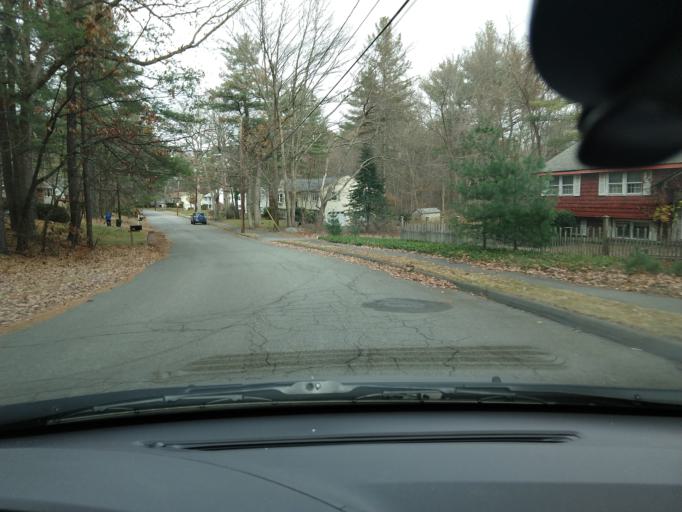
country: US
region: Massachusetts
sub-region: Middlesex County
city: Bedford
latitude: 42.5029
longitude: -71.2479
